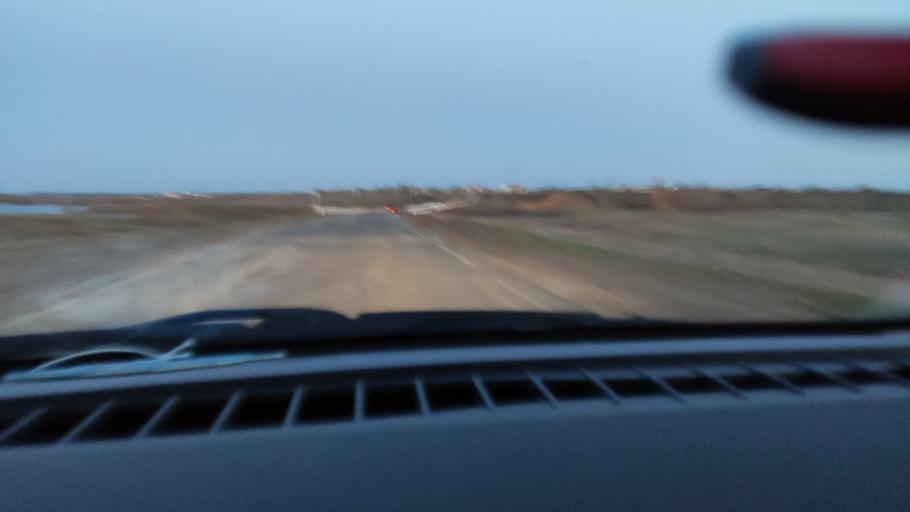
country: RU
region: Saratov
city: Rovnoye
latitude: 51.0302
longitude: 46.0882
